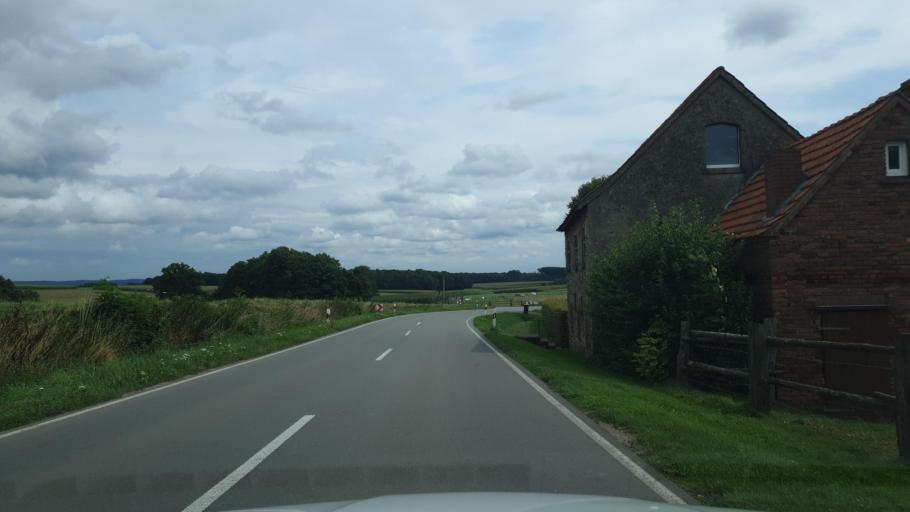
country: DE
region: Lower Saxony
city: Bissendorf
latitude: 52.1834
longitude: 8.2130
